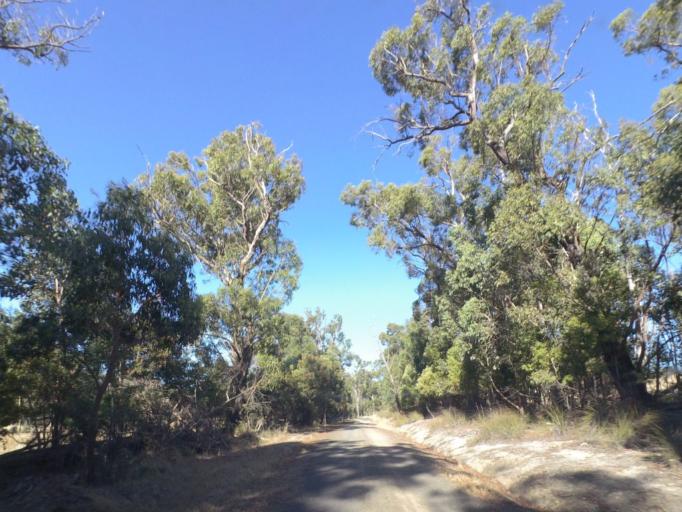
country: AU
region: Victoria
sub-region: Murrindindi
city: Kinglake West
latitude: -37.4602
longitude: 145.3907
